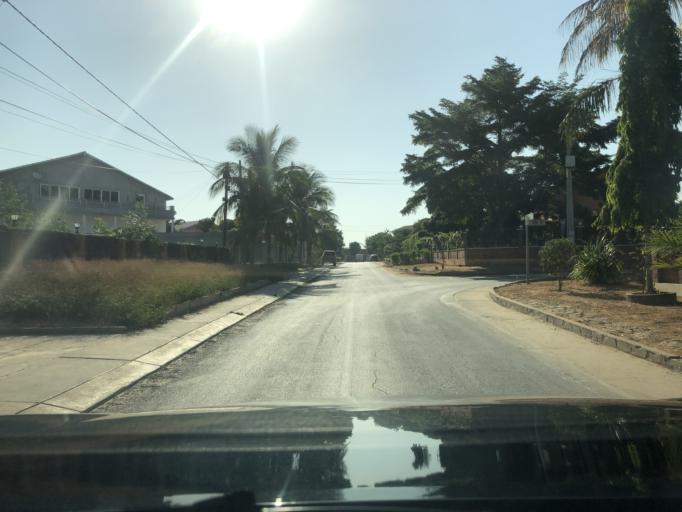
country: AO
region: Luanda
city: Luanda
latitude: -8.9082
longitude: 13.2258
